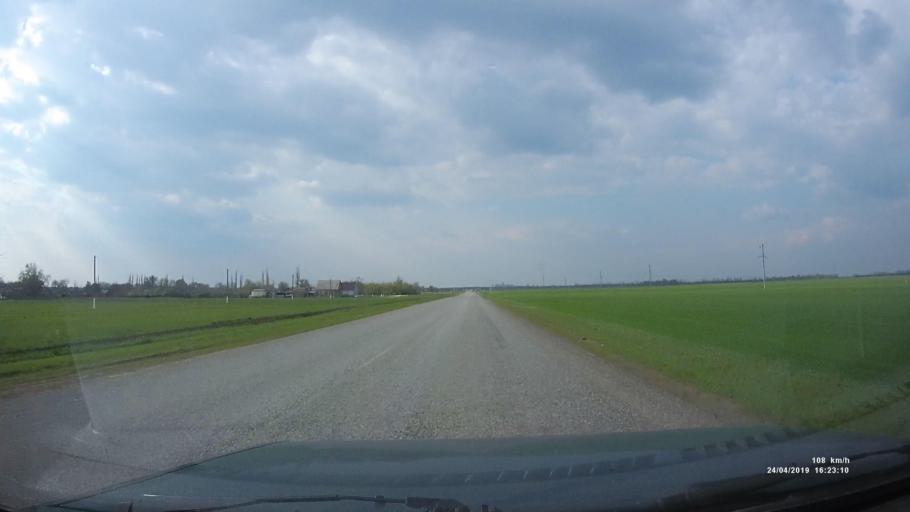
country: RU
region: Rostov
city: Orlovskiy
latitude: 46.8305
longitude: 42.0512
